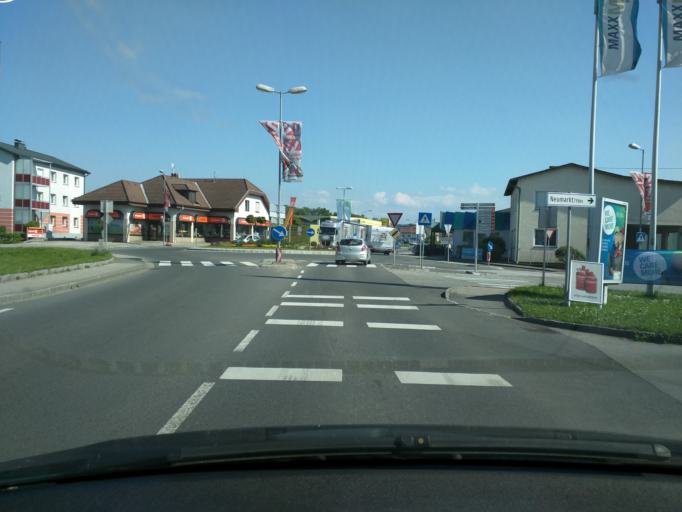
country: AT
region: Lower Austria
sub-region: Politischer Bezirk Melk
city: Ybbs an der Donau
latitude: 48.1712
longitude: 15.0848
